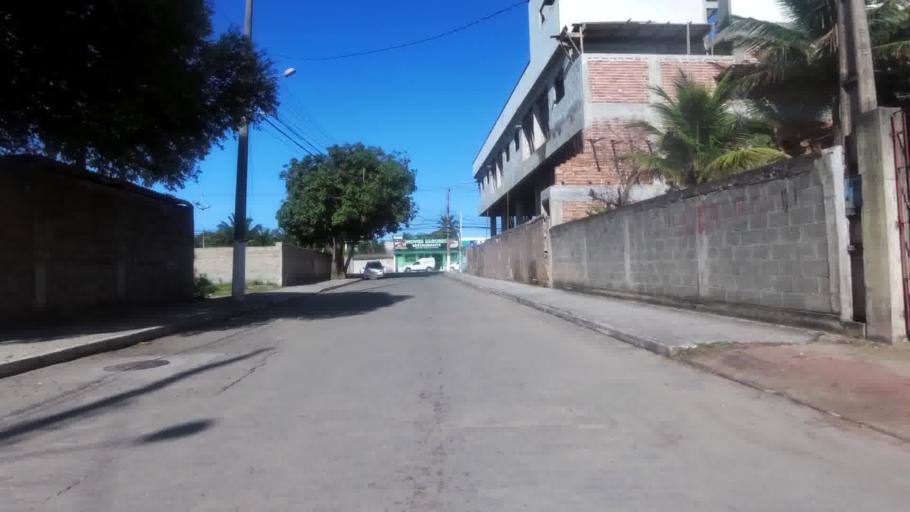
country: BR
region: Espirito Santo
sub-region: Piuma
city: Piuma
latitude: -20.8126
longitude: -40.6321
